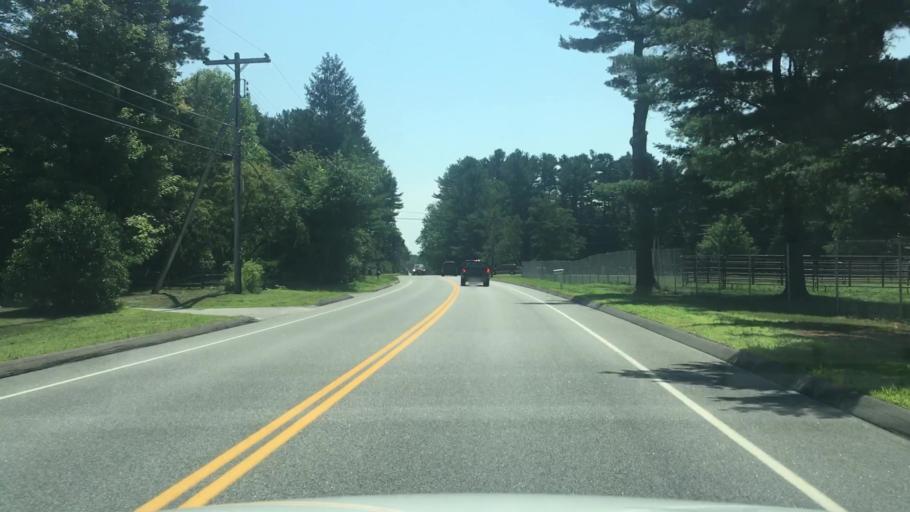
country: US
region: Maine
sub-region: Cumberland County
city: Cumberland Center
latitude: 43.8107
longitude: -70.2868
